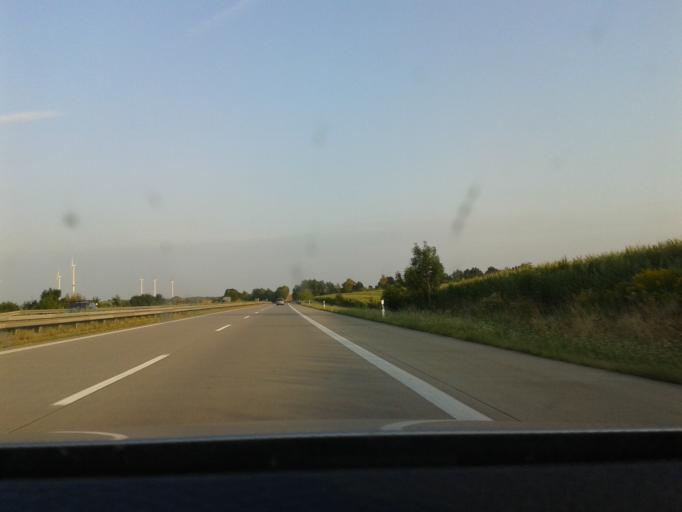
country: DE
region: Saxony
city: Mochau
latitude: 51.1429
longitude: 13.1488
